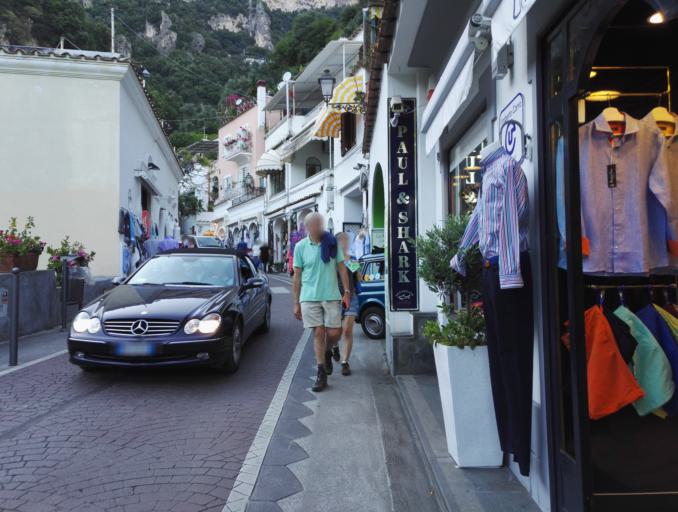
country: IT
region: Campania
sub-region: Provincia di Salerno
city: Positano
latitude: 40.6306
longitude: 14.4853
